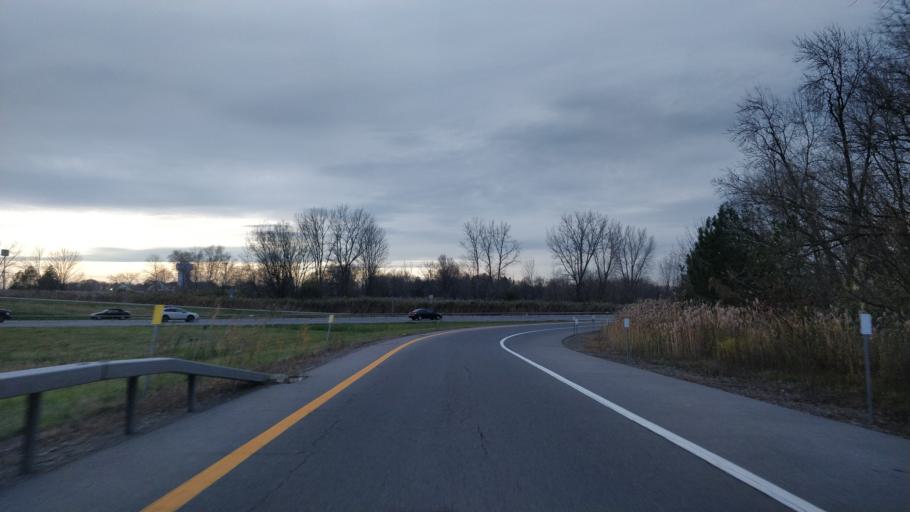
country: US
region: New York
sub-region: Onondaga County
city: Brewerton
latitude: 43.2329
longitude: -76.1278
